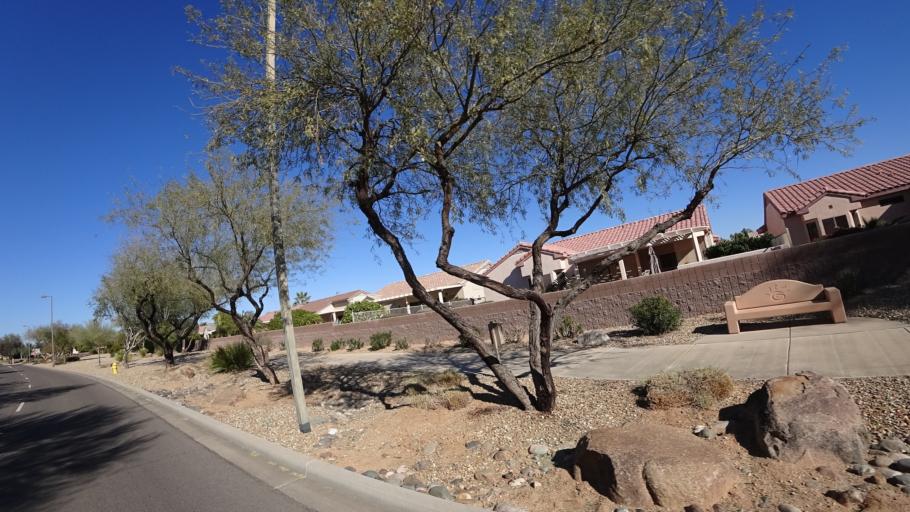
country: US
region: Arizona
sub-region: Maricopa County
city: Sun City West
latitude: 33.6549
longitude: -112.4130
